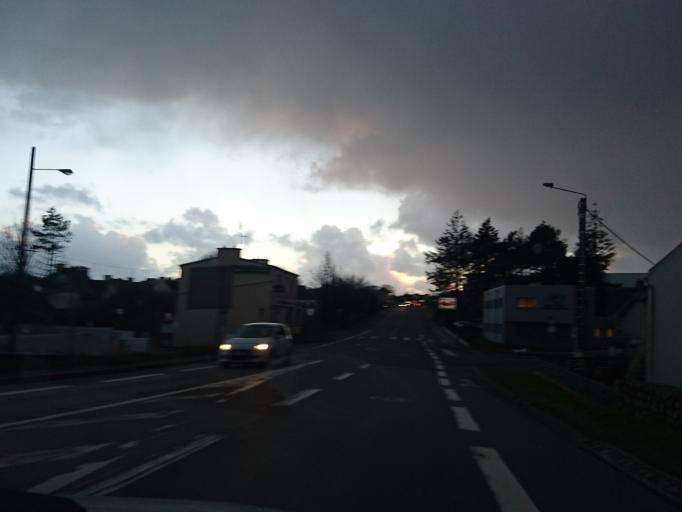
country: FR
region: Brittany
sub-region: Departement du Finistere
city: Guipavas
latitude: 48.4169
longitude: -4.4322
